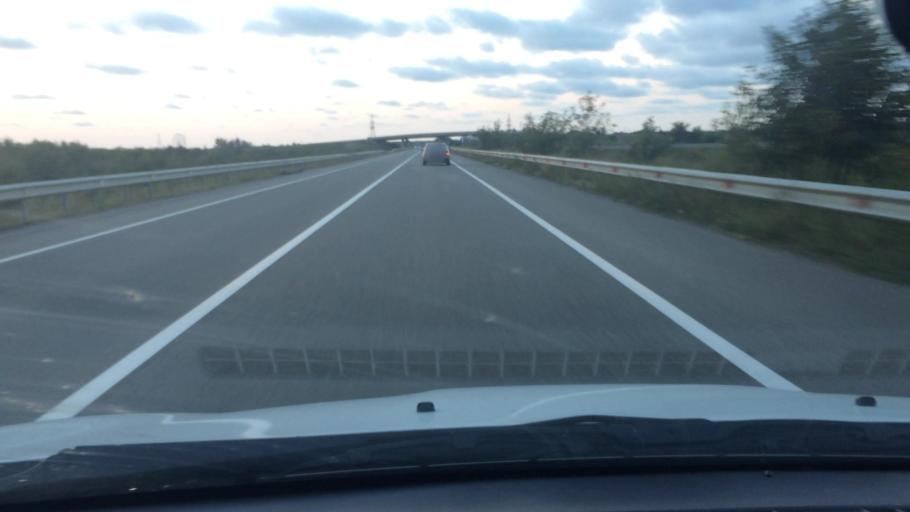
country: GE
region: Ajaria
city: Ochkhamuri
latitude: 41.8958
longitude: 41.8006
